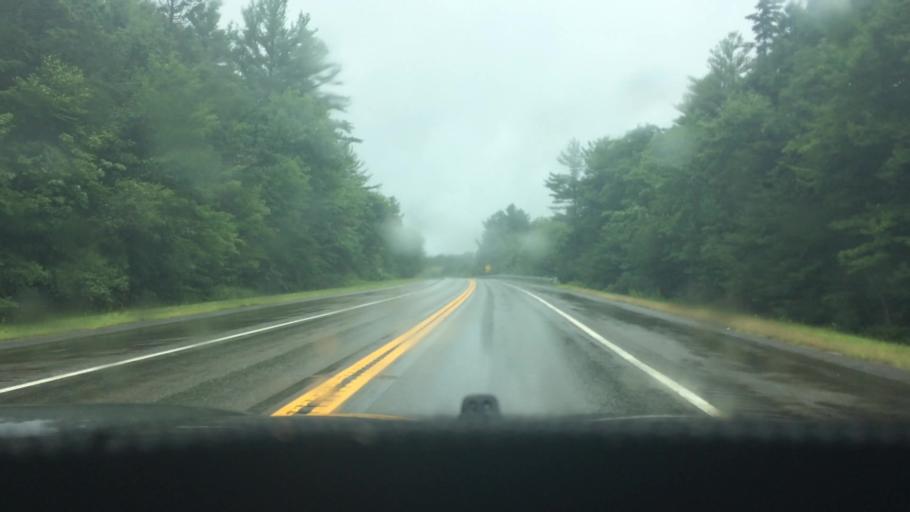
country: US
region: Massachusetts
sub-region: Worcester County
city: South Ashburnham
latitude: 42.5818
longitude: -71.9532
